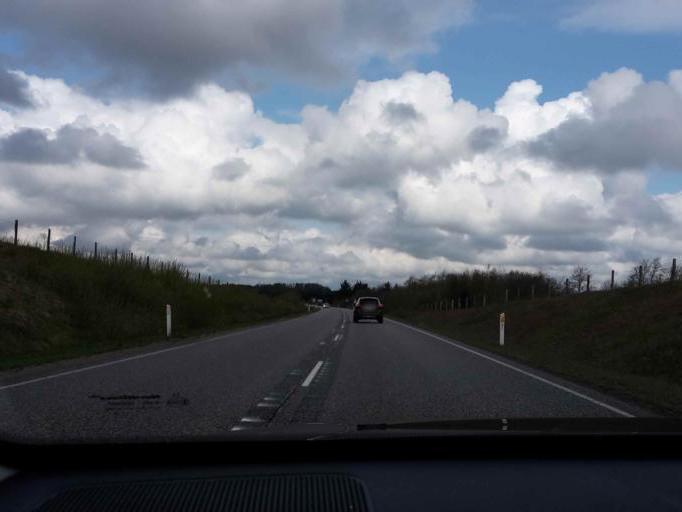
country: DK
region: South Denmark
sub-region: Billund Kommune
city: Billund
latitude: 55.7422
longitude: 9.1940
